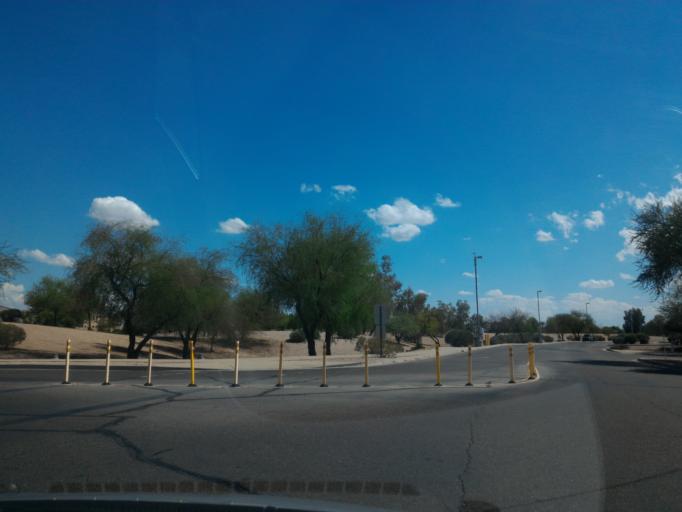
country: US
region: Arizona
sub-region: Maricopa County
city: Sun Lakes
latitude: 33.2431
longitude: -111.8783
